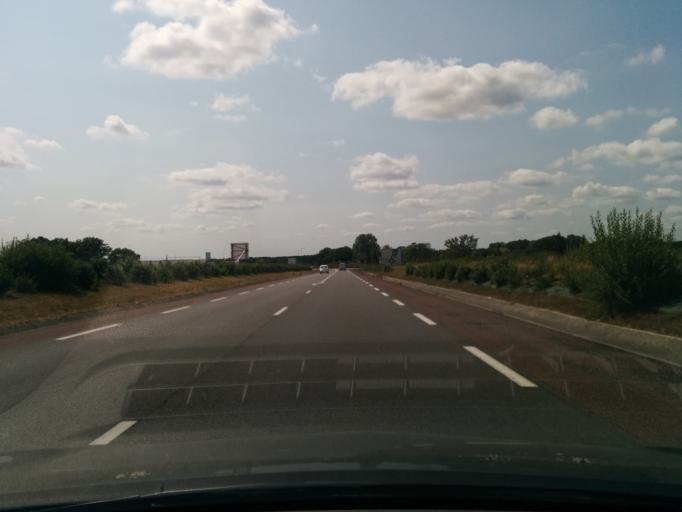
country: FR
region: Centre
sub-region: Departement du Cher
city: Vierzon
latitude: 47.2448
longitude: 2.0796
